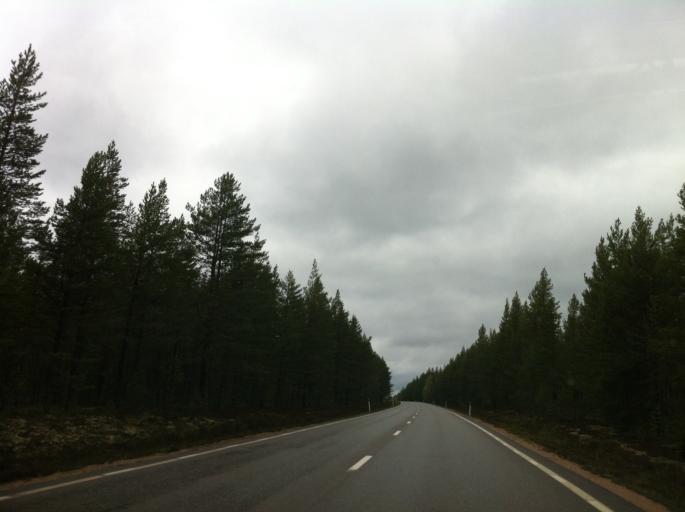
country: SE
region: Jaemtland
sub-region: Harjedalens Kommun
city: Sveg
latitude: 62.0579
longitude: 14.2959
